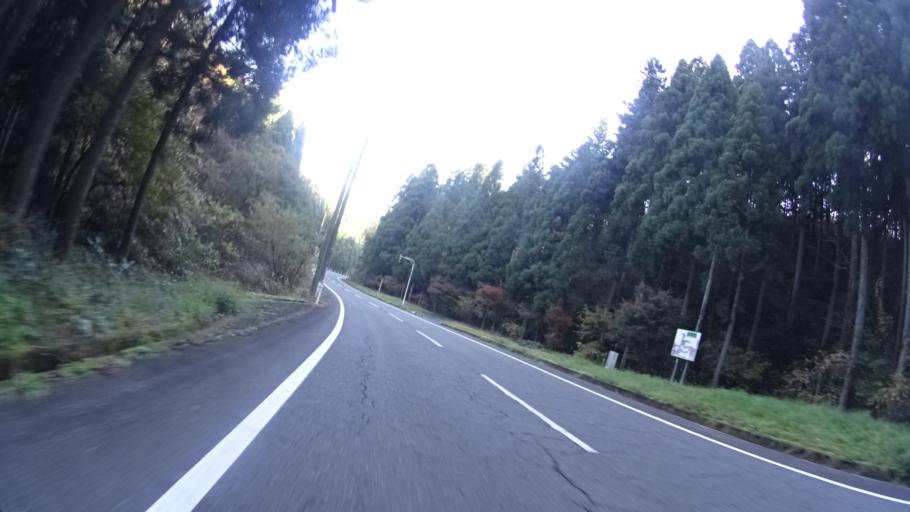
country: JP
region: Fukui
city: Maruoka
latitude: 36.1463
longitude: 136.3276
